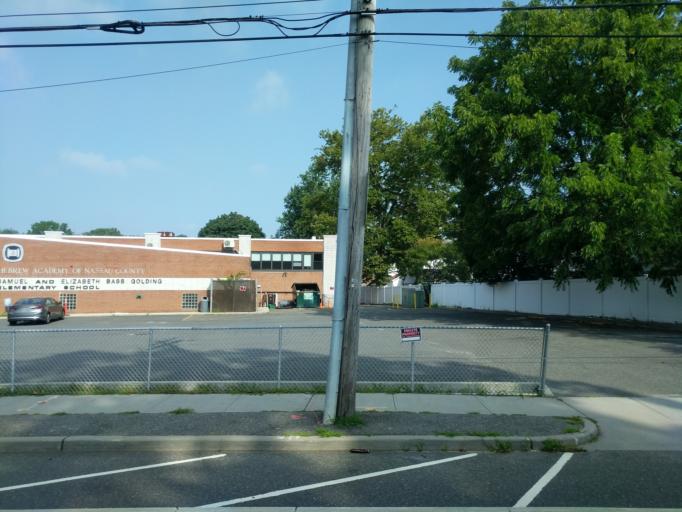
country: US
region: New York
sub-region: Nassau County
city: Lakeview
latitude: 40.6935
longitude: -73.6570
